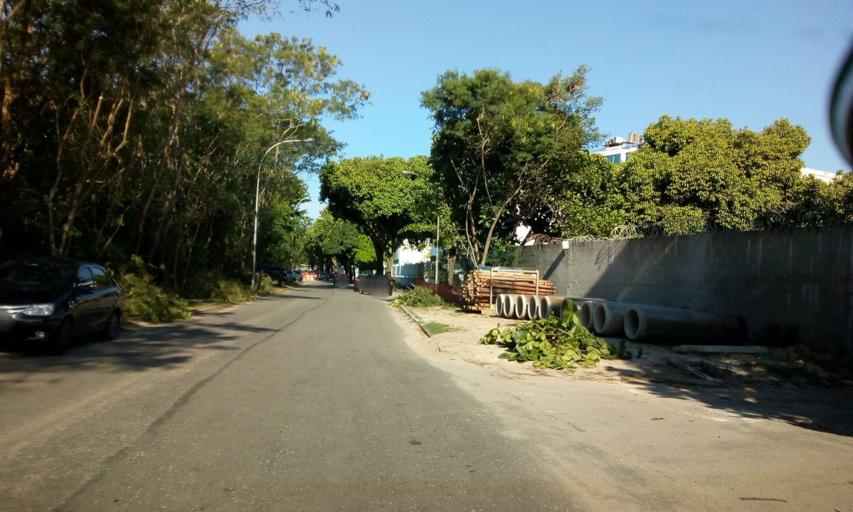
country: BR
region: Rio de Janeiro
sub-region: Nilopolis
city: Nilopolis
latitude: -22.9949
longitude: -43.3816
